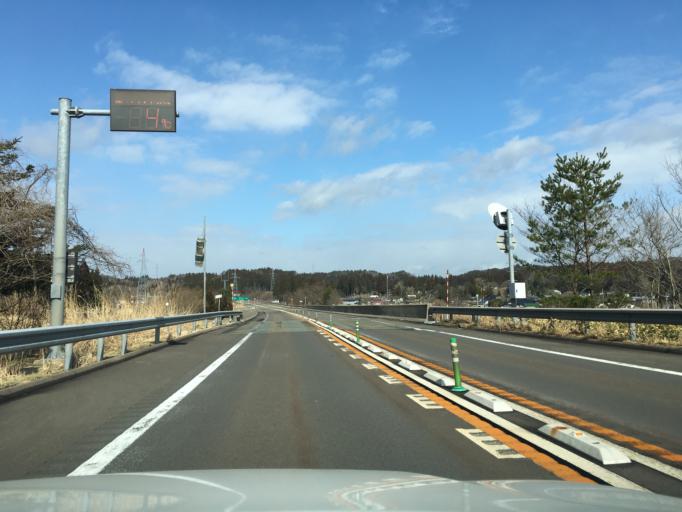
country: JP
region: Akita
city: Akita
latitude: 39.7355
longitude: 140.1749
